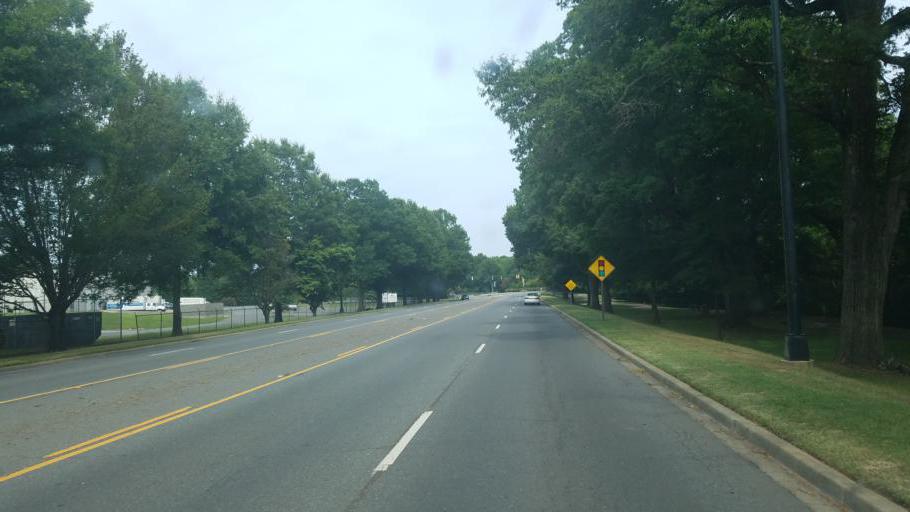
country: US
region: South Carolina
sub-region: York County
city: Rock Hill
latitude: 34.9344
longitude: -81.0061
